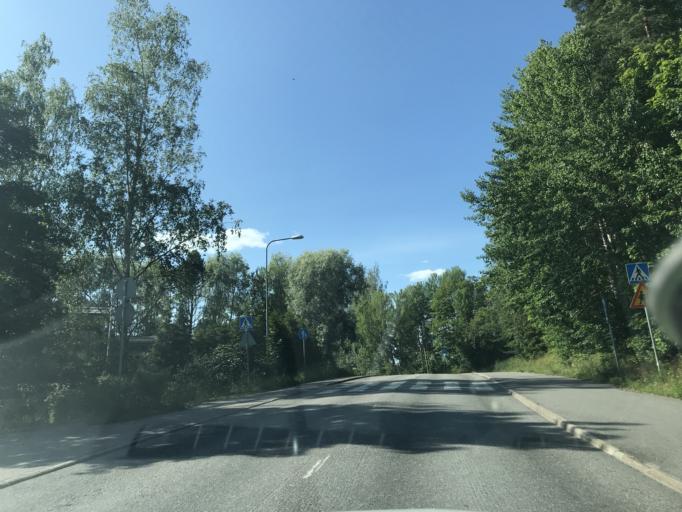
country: FI
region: Uusimaa
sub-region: Helsinki
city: Nurmijaervi
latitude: 60.3784
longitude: 24.7488
